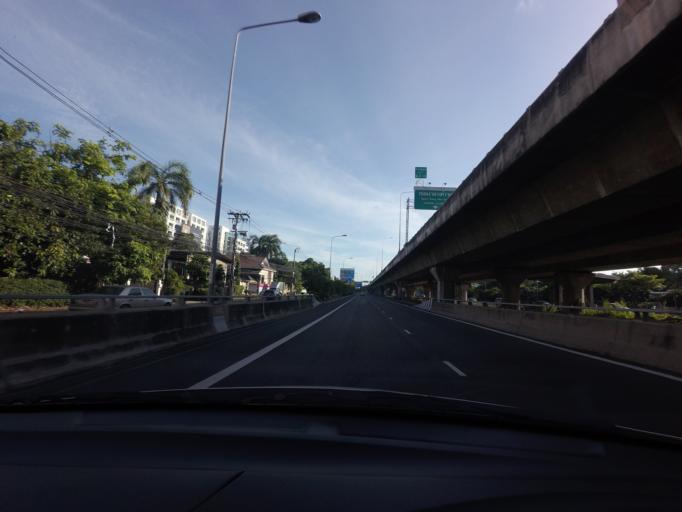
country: TH
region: Nonthaburi
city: Mueang Nonthaburi
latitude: 13.8518
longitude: 100.5332
